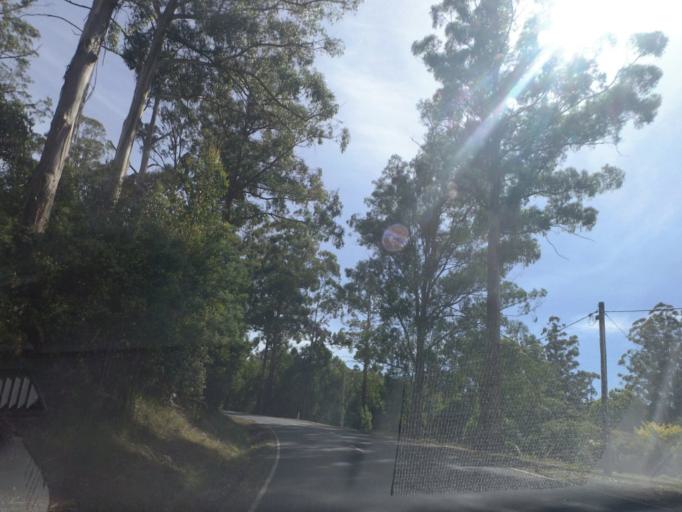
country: AU
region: Victoria
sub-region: Nillumbik
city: Saint Andrews
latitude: -37.5286
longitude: 145.3455
